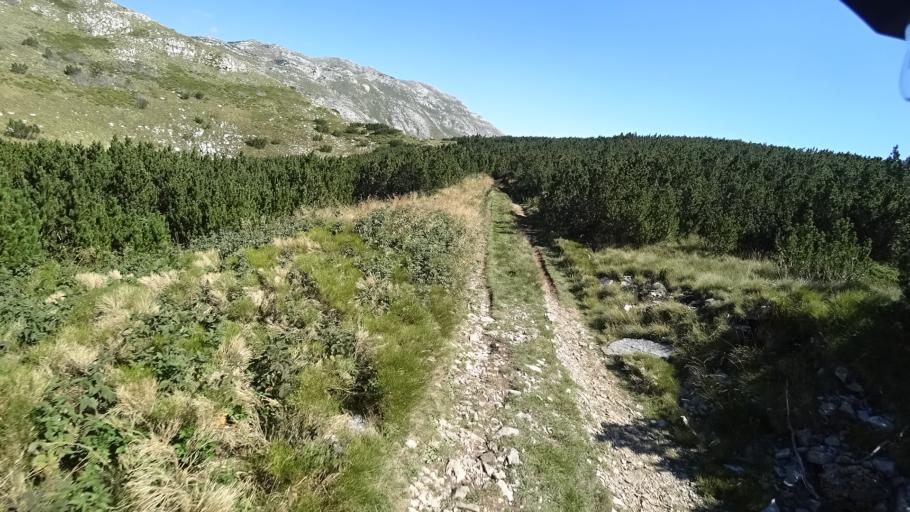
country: HR
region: Splitsko-Dalmatinska
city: Hrvace
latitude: 43.9365
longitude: 16.5734
